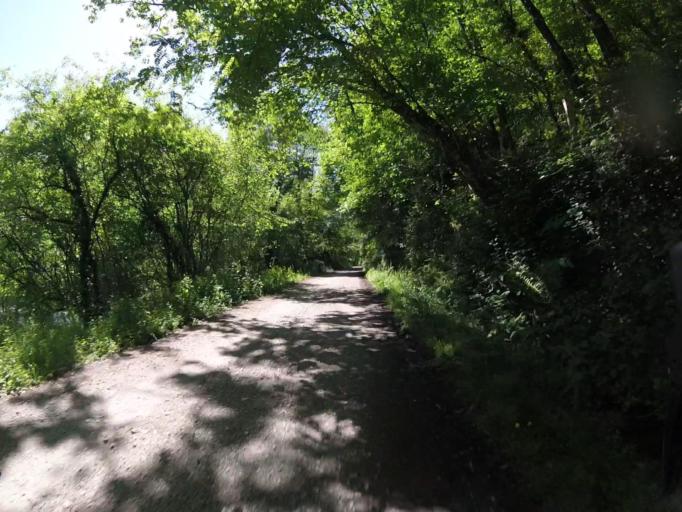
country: ES
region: Navarre
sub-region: Provincia de Navarra
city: Bera
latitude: 43.2788
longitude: -1.7138
